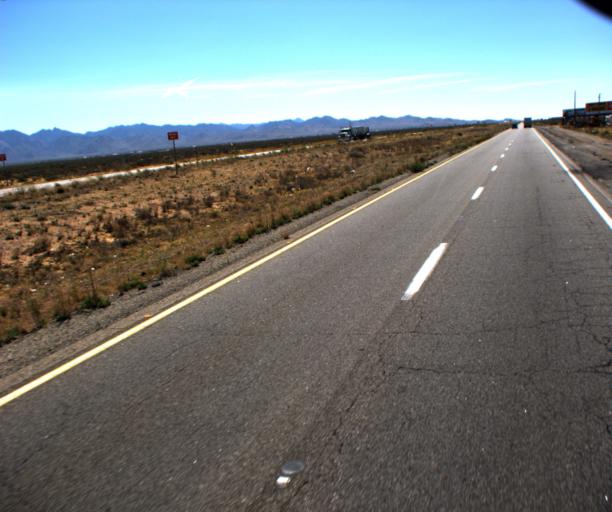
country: US
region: Arizona
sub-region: Mohave County
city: Dolan Springs
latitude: 35.5605
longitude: -114.3740
